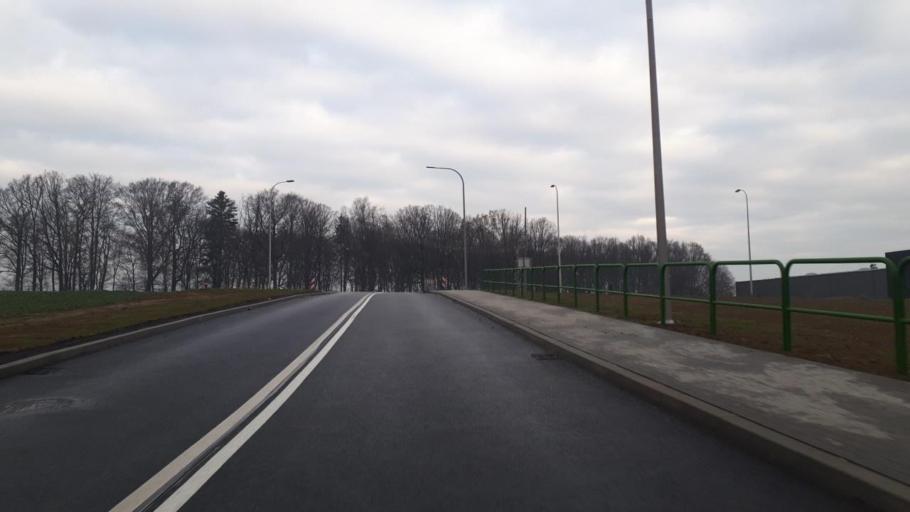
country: PL
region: Silesian Voivodeship
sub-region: Powiat bielski
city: Bronow
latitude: 49.8606
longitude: 18.9267
